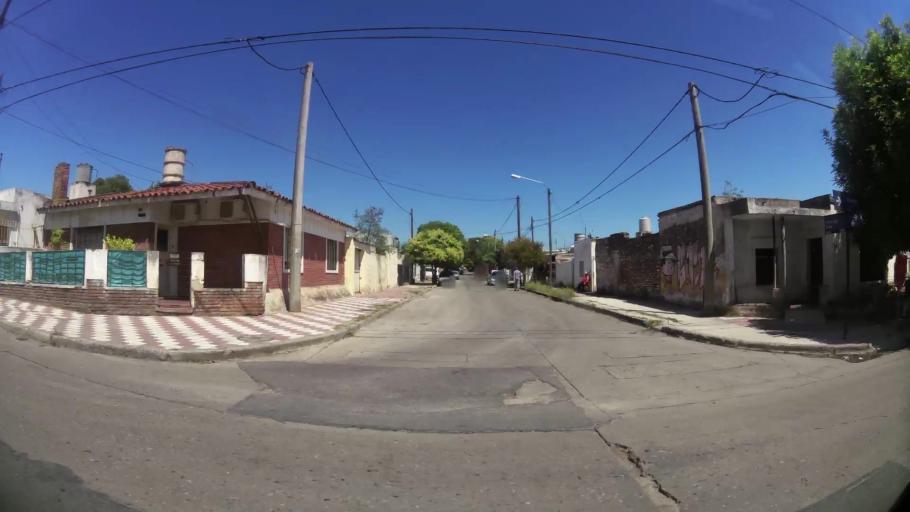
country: AR
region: Cordoba
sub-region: Departamento de Capital
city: Cordoba
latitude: -31.4217
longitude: -64.2090
